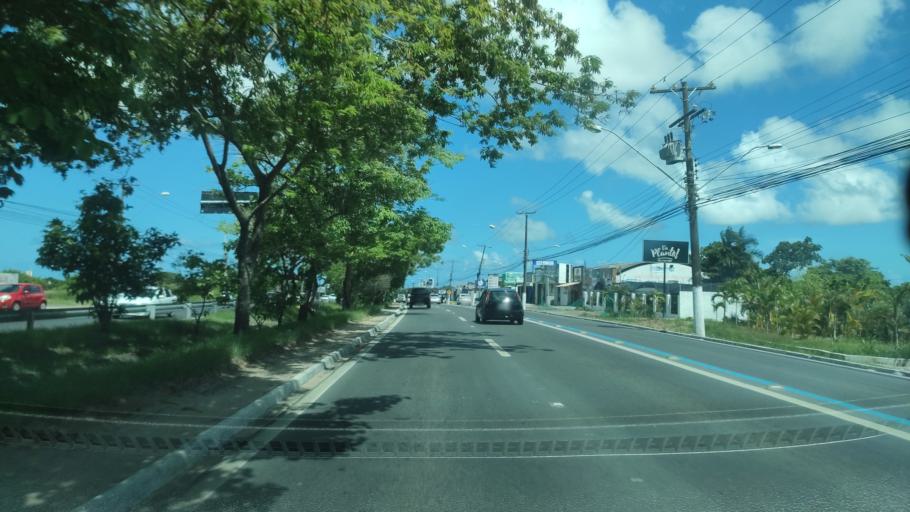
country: BR
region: Alagoas
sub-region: Maceio
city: Maceio
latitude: -9.5977
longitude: -35.7505
